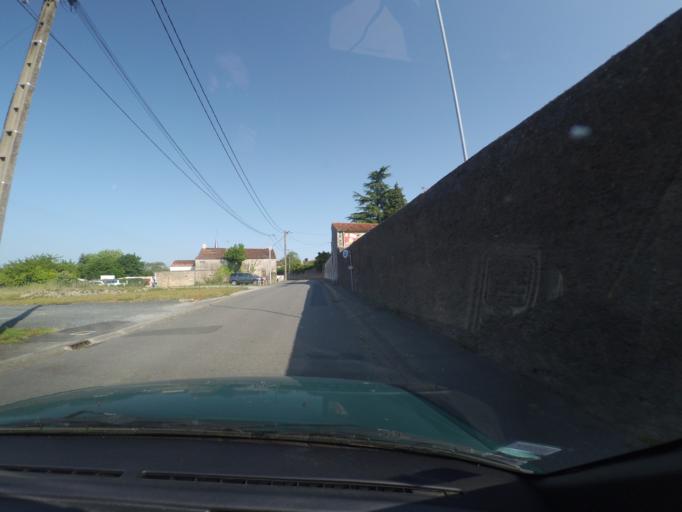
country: FR
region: Pays de la Loire
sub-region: Departement de la Loire-Atlantique
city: Maisdon-sur-Sevre
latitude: 47.0965
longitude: -1.3823
